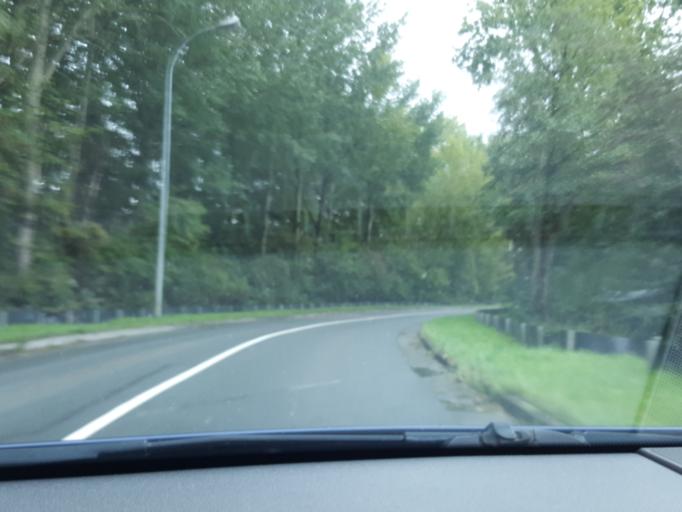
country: DE
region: Lower Saxony
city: Emden
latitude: 53.3364
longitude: 7.2228
